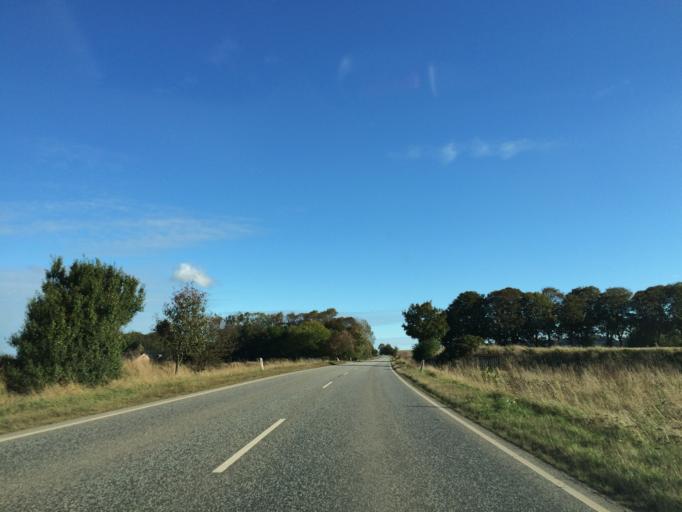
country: DK
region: Central Jutland
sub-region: Randers Kommune
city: Langa
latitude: 56.3762
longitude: 9.9451
